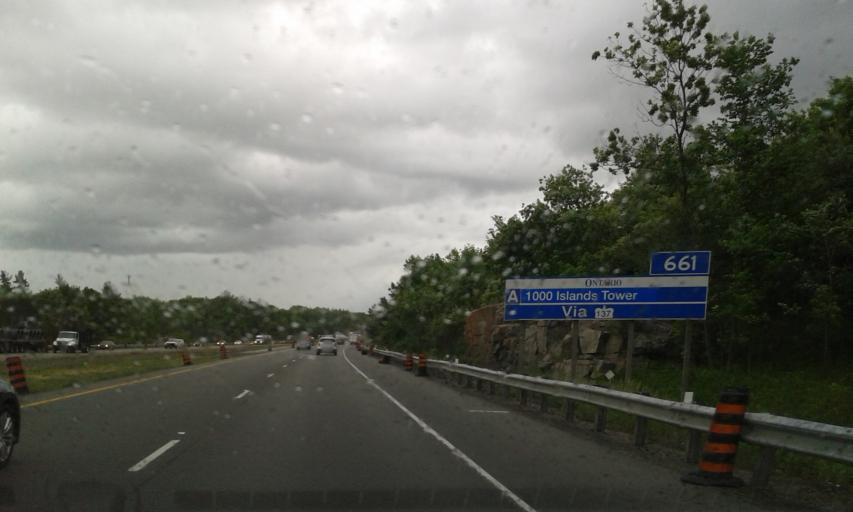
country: US
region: New York
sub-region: Jefferson County
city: Alexandria Bay
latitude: 44.3784
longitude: -76.0290
